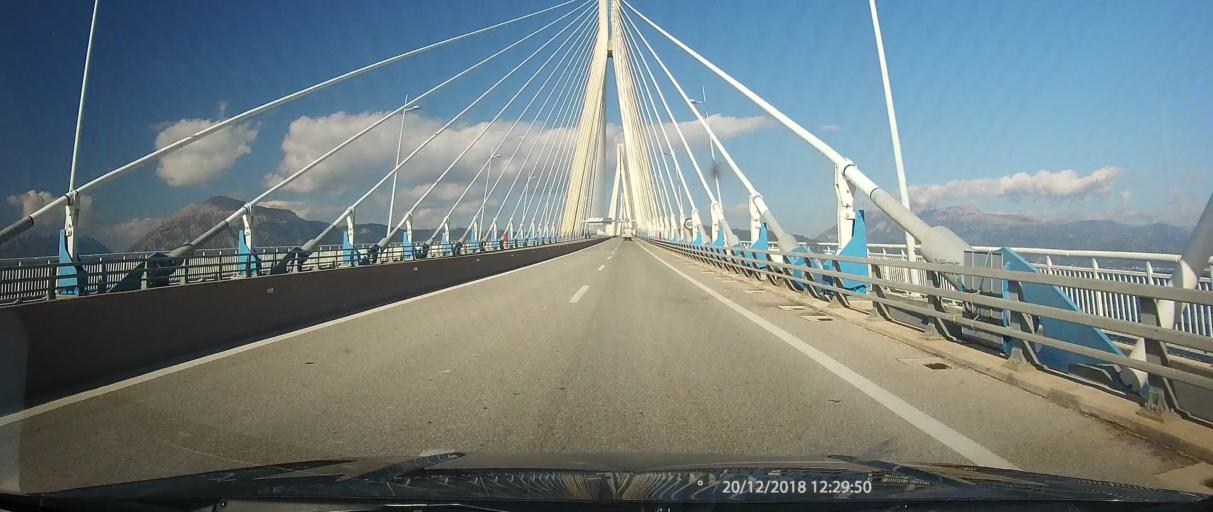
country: GR
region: West Greece
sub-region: Nomos Achaias
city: Rio
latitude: 38.3112
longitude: 21.7784
